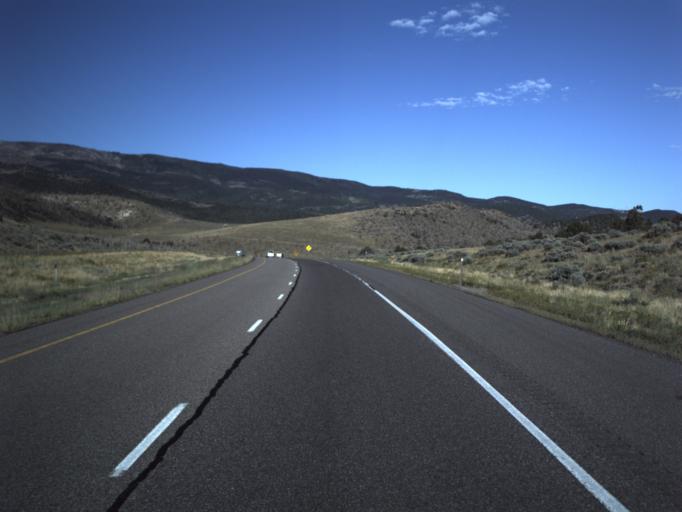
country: US
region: Utah
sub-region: Sevier County
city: Monroe
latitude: 38.5540
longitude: -112.4147
